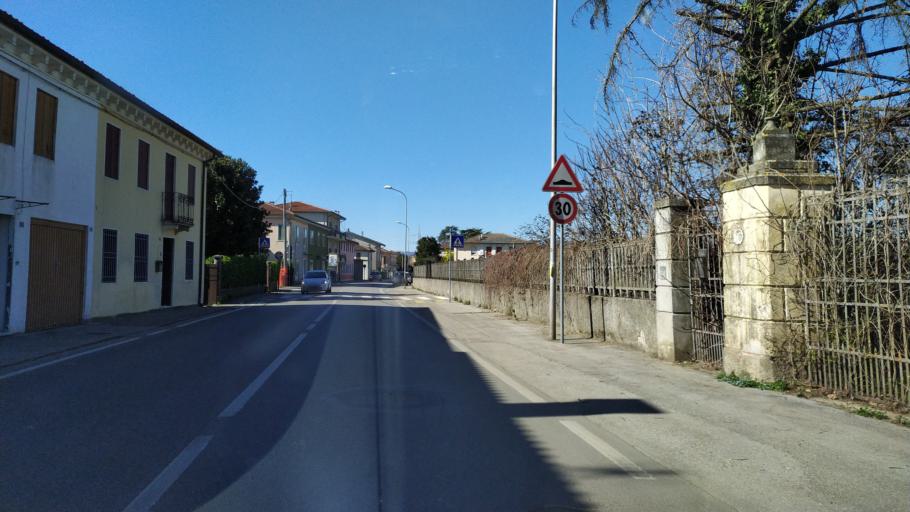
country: IT
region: Veneto
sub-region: Provincia di Vicenza
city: Vigardolo
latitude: 45.6085
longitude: 11.5776
